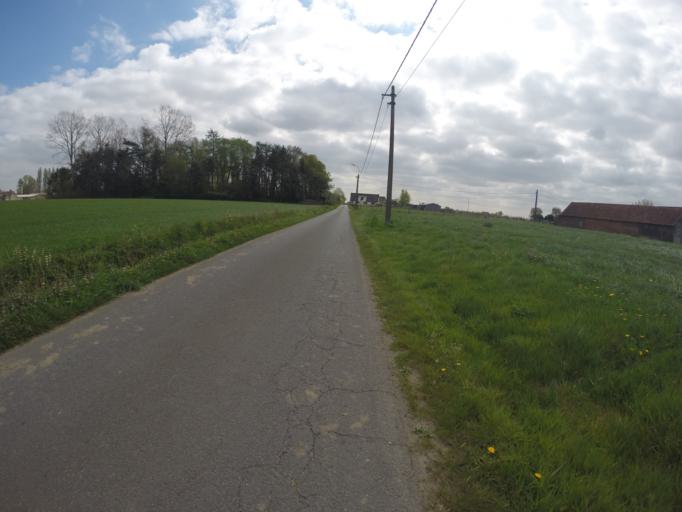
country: BE
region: Flanders
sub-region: Provincie Oost-Vlaanderen
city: Aalter
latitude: 51.0454
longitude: 3.4840
